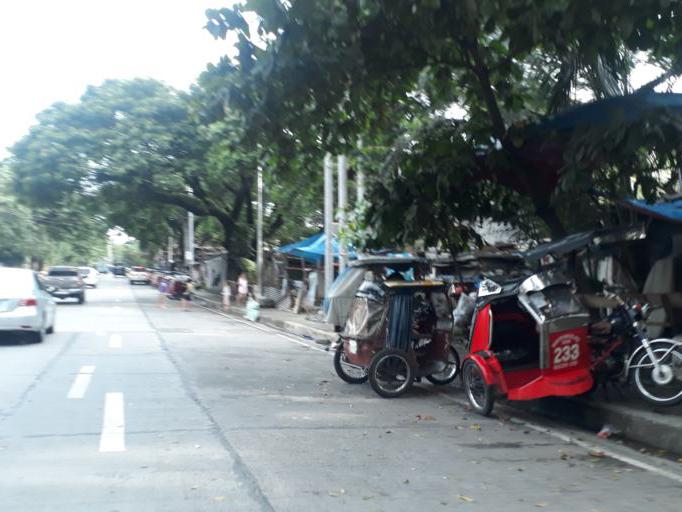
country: PH
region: Metro Manila
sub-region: Quezon City
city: Quezon City
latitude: 14.6500
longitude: 121.0594
